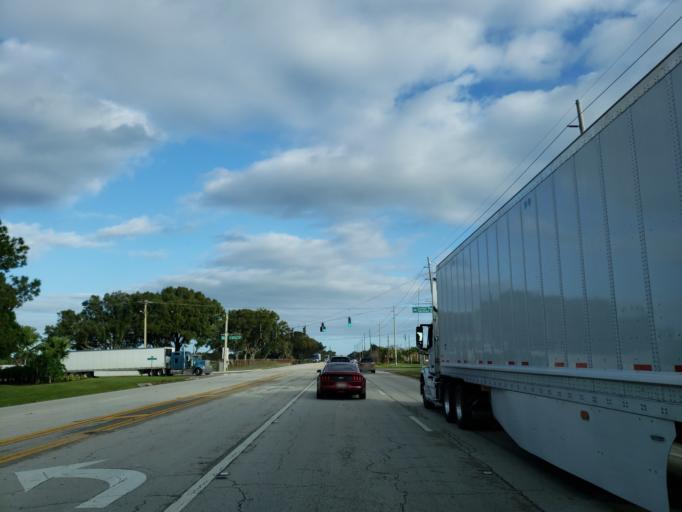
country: US
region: Florida
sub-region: Hillsborough County
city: Plant City
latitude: 28.0005
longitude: -82.1050
